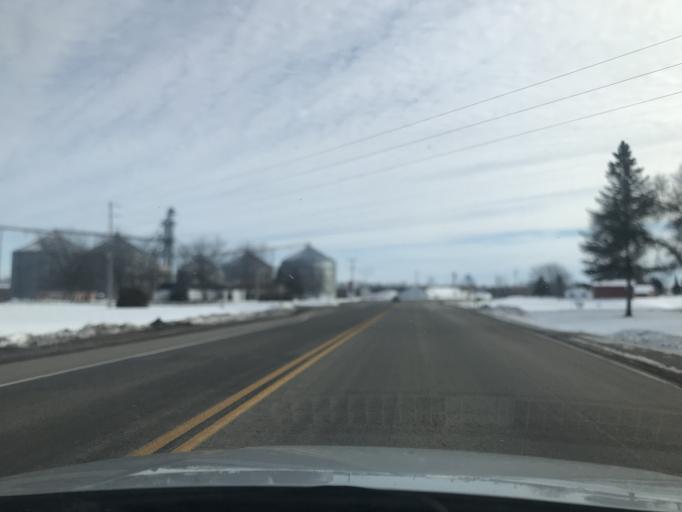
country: US
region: Wisconsin
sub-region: Oconto County
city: Oconto Falls
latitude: 44.8854
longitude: -88.1574
